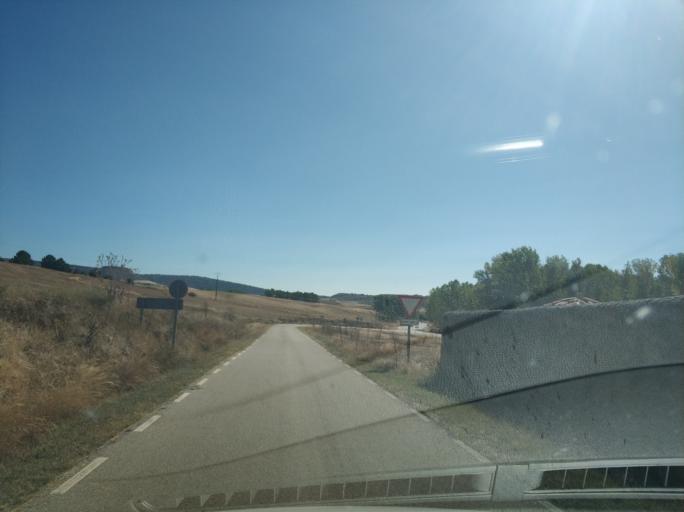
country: ES
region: Castille and Leon
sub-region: Provincia de Soria
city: Santa Maria de las Hoyas
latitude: 41.7704
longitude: -3.1679
